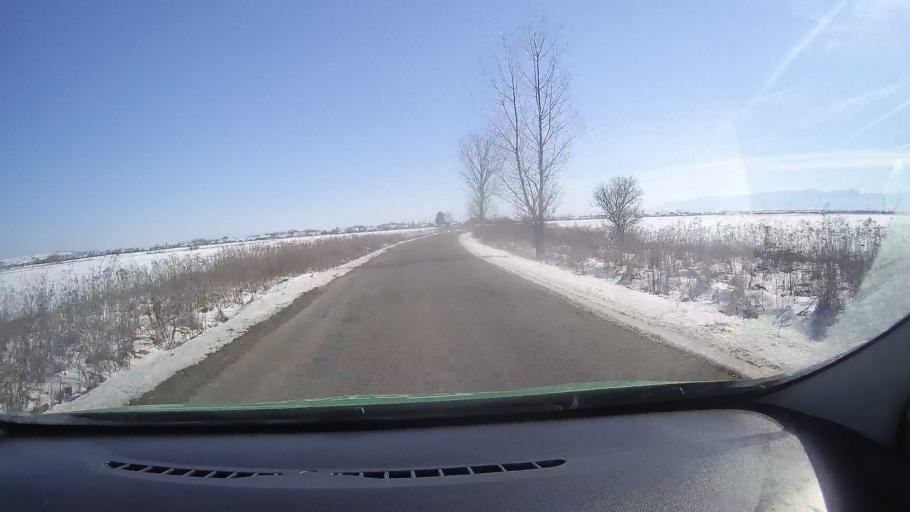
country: RO
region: Brasov
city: Fogarasch
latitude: 45.8176
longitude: 24.9930
